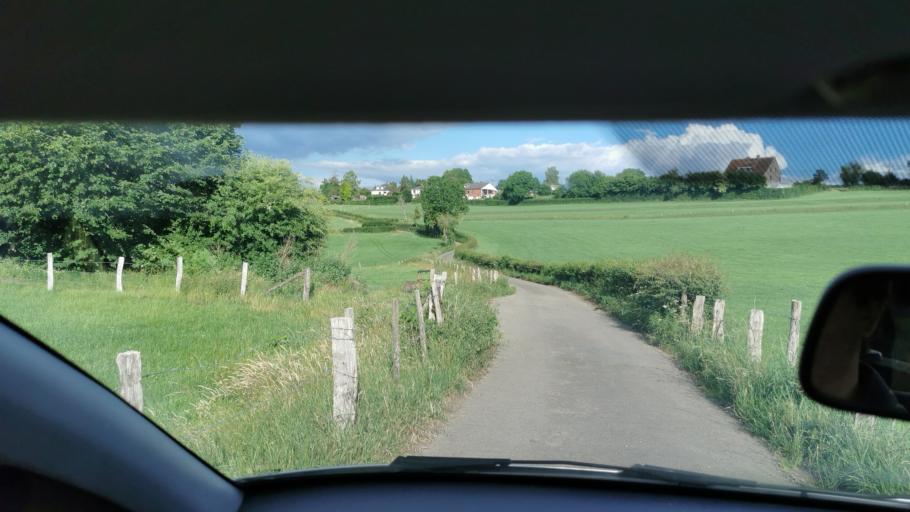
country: BE
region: Wallonia
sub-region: Province de Liege
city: Theux
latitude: 50.5372
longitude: 5.7997
